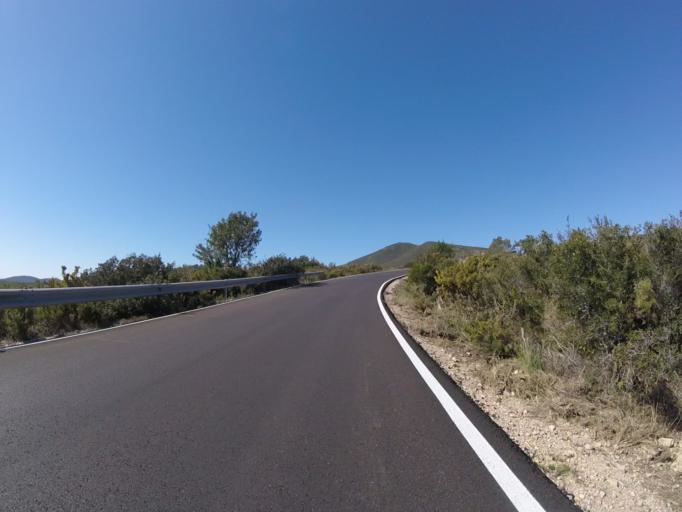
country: ES
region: Valencia
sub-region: Provincia de Castello
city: Cervera del Maestre
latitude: 40.4005
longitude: 0.2355
